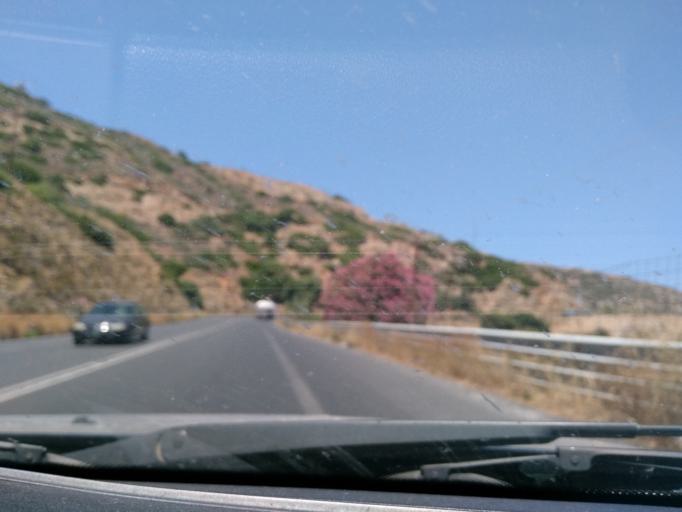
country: GR
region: Crete
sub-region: Nomos Irakleiou
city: Gazi
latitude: 35.3750
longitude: 25.0363
